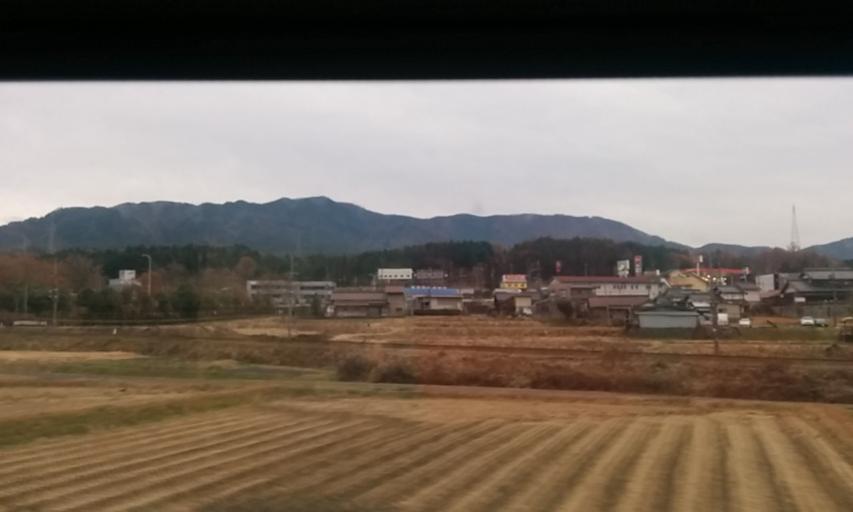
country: JP
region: Gifu
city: Nakatsugawa
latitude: 35.4780
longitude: 137.4794
